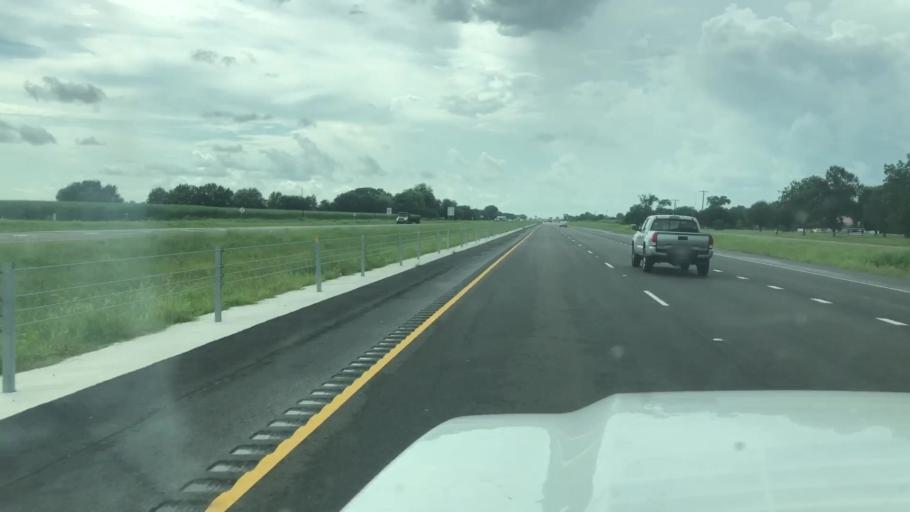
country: US
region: Louisiana
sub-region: Iberia Parish
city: Jeanerette
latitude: 29.8694
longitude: -91.6391
